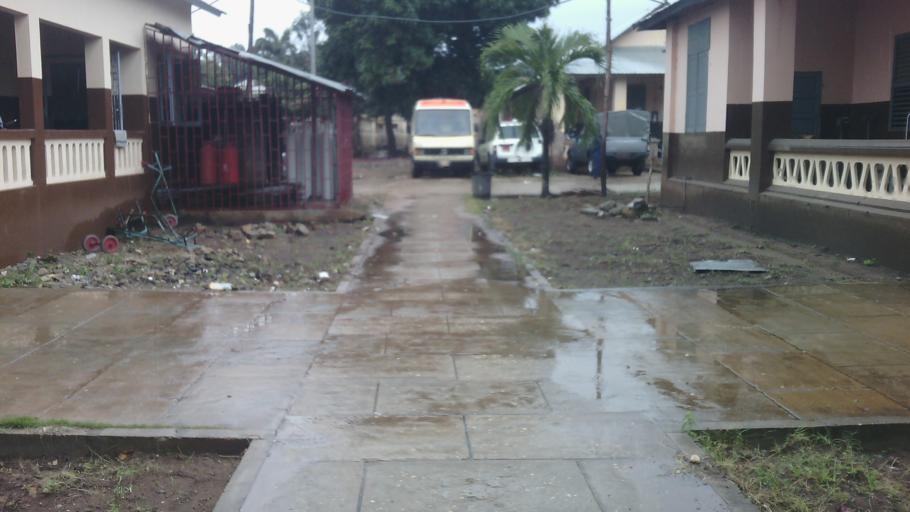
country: BJ
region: Queme
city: Porto-Novo
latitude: 6.4745
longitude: 2.6127
